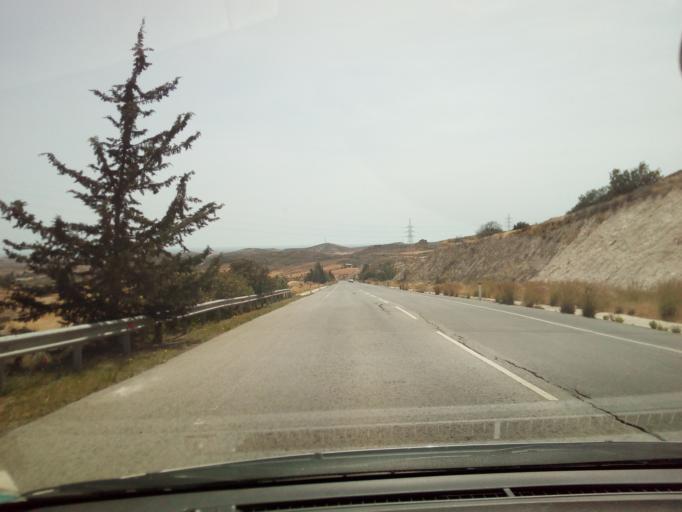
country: CY
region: Larnaka
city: Athienou
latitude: 35.0180
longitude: 33.5554
